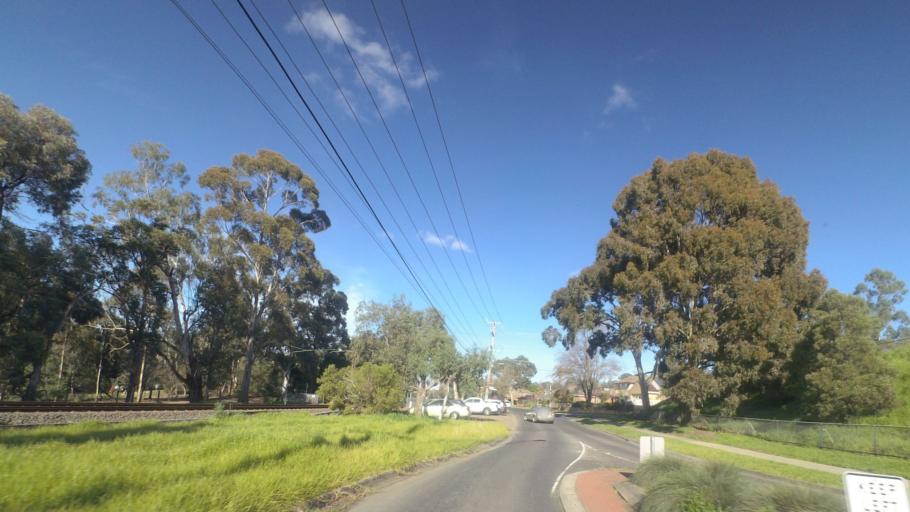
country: AU
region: Victoria
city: Macleod
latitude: -37.7354
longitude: 145.0656
